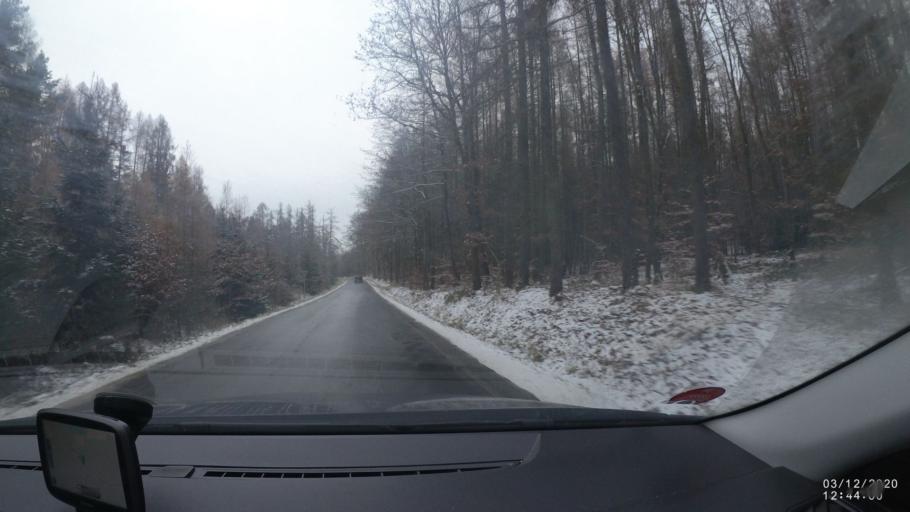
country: CZ
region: Central Bohemia
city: Revnicov
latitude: 50.1689
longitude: 13.8427
